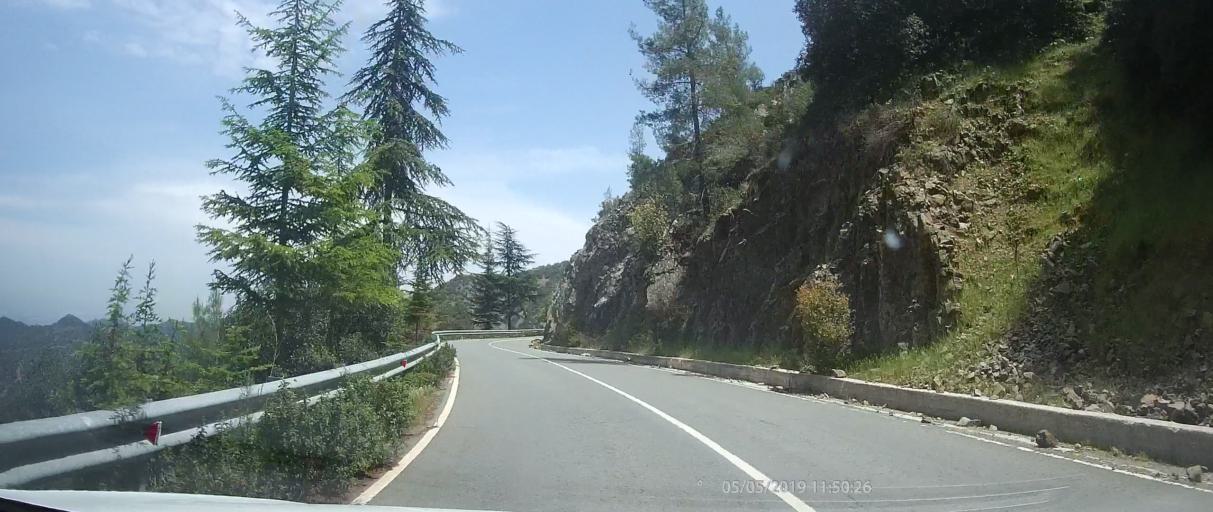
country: CY
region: Lefkosia
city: Kato Pyrgos
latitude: 34.9980
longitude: 32.6937
